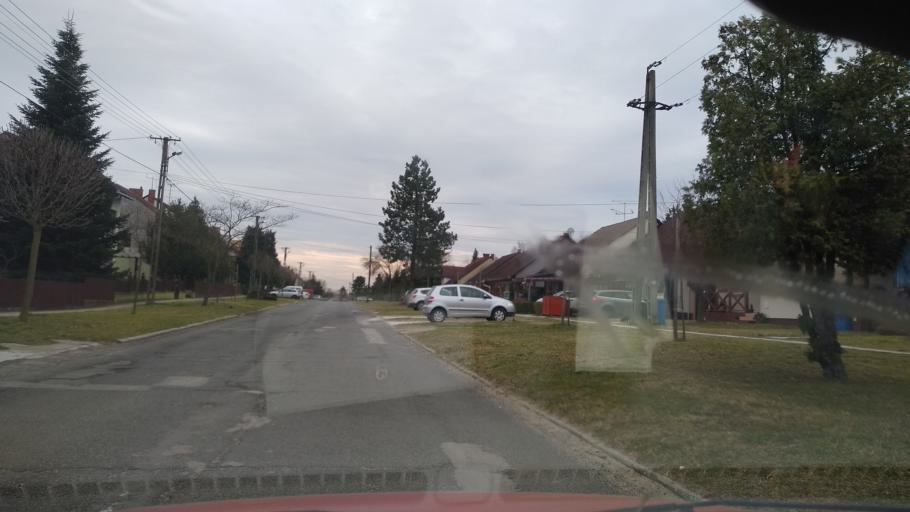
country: HU
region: Somogy
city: Barcs
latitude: 45.9638
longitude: 17.4715
